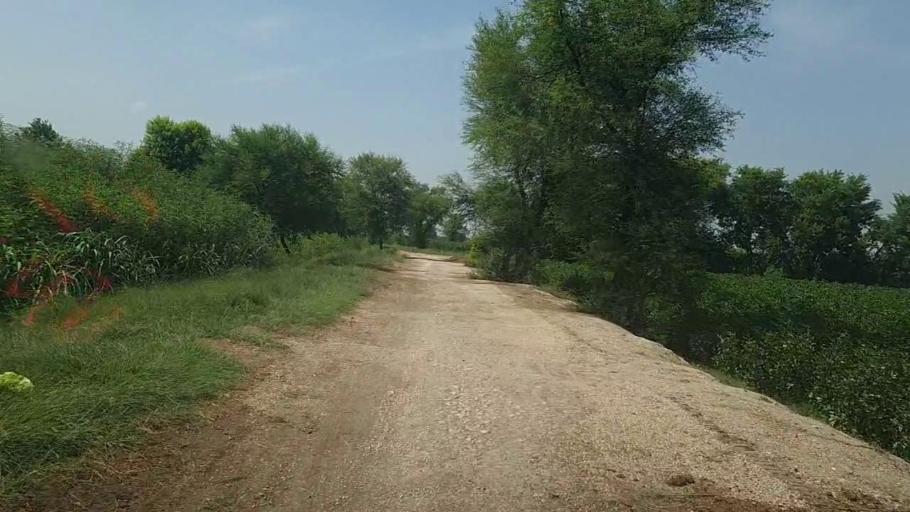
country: PK
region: Sindh
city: Ubauro
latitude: 28.1749
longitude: 69.8150
